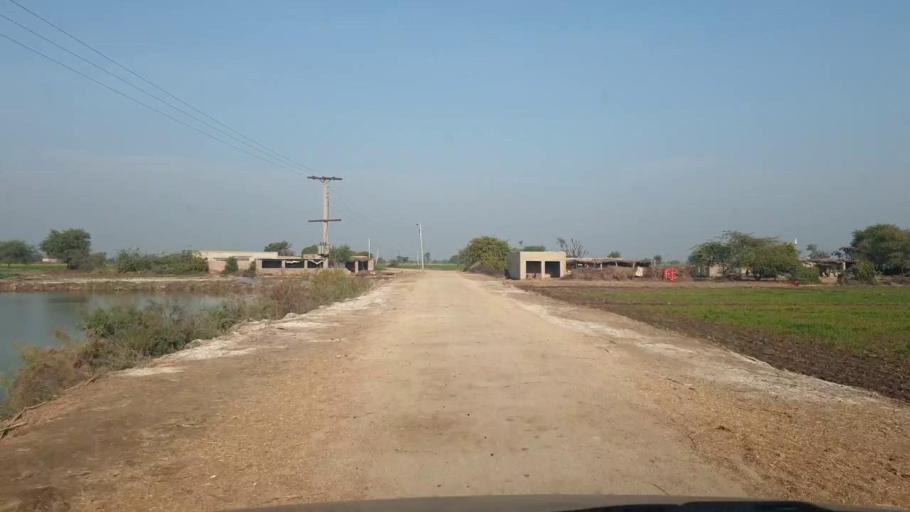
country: PK
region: Sindh
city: Tando Adam
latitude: 25.7321
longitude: 68.6072
